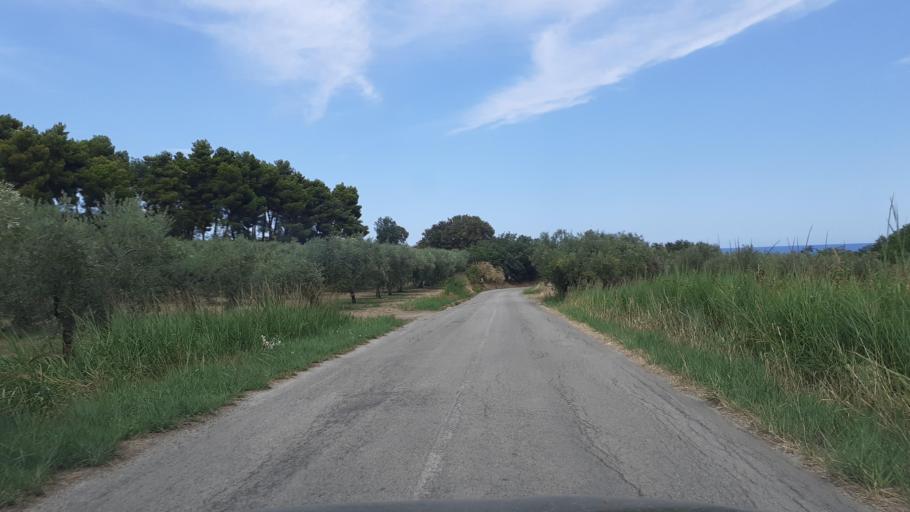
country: IT
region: Abruzzo
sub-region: Provincia di Chieti
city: Fossacesia
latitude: 42.2547
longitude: 14.5000
